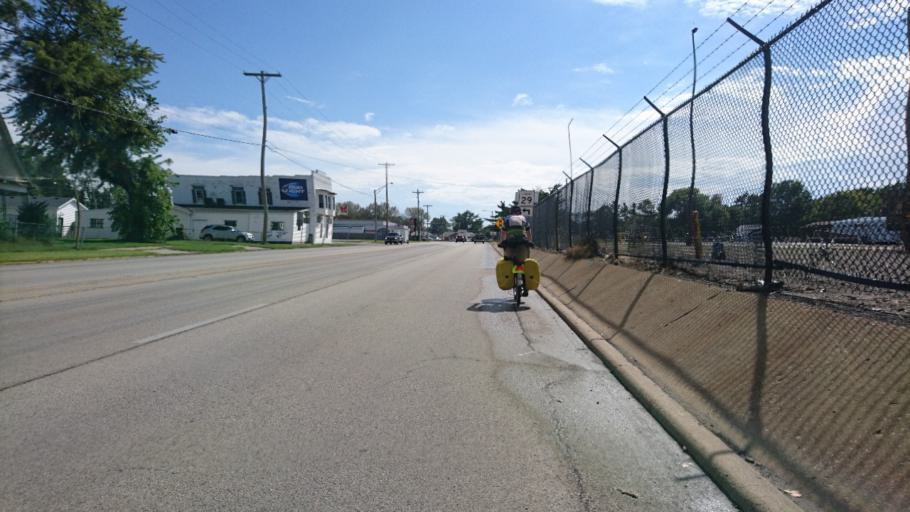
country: US
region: Illinois
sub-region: Sangamon County
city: Grandview
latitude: 39.8331
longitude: -89.6359
